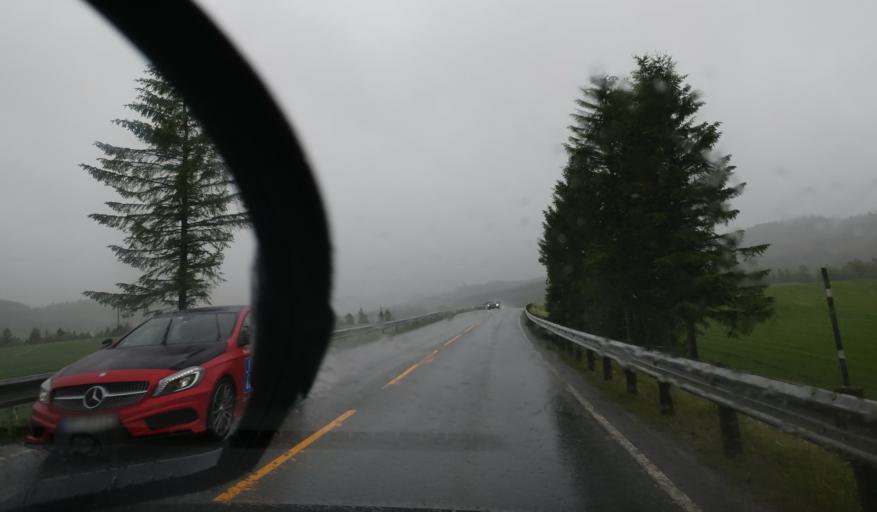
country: NO
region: Nord-Trondelag
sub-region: Stjordal
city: Stjordalshalsen
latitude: 63.4062
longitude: 10.9413
